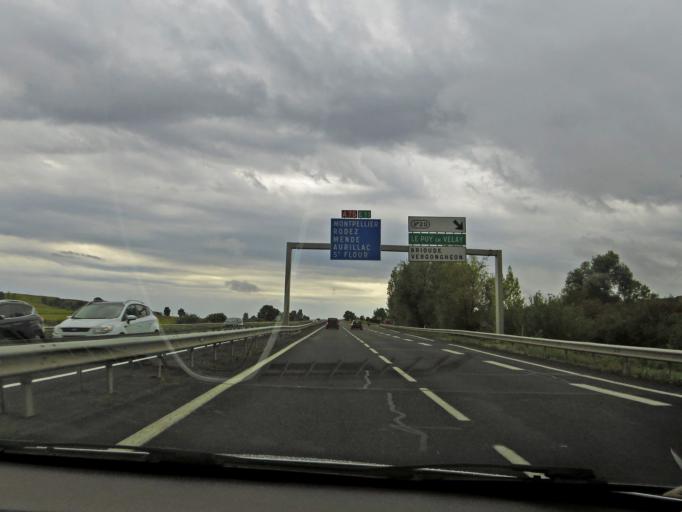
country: FR
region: Auvergne
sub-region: Departement de la Haute-Loire
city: Lempdes-sur-Allagnon
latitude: 45.3813
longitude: 3.2806
